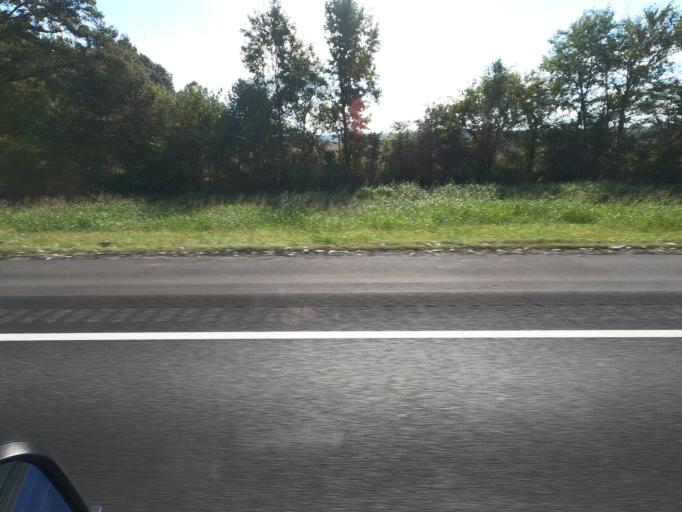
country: US
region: Tennessee
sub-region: Fayette County
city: Hickory Withe
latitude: 35.3096
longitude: -89.5853
